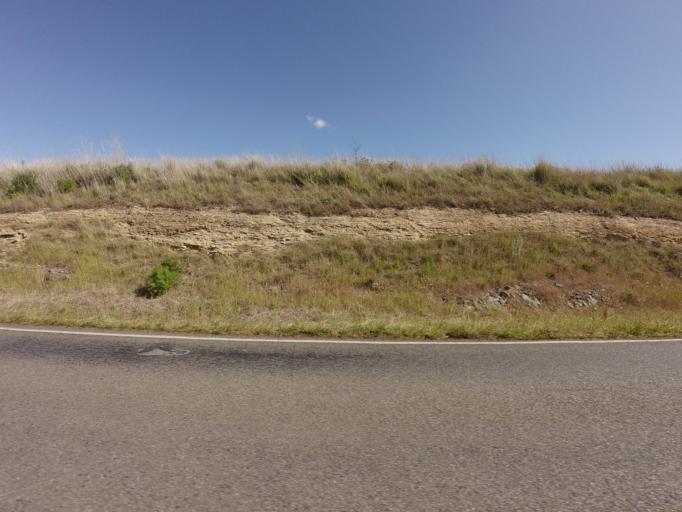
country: AU
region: Tasmania
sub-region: Derwent Valley
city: New Norfolk
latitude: -42.6510
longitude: 146.9316
